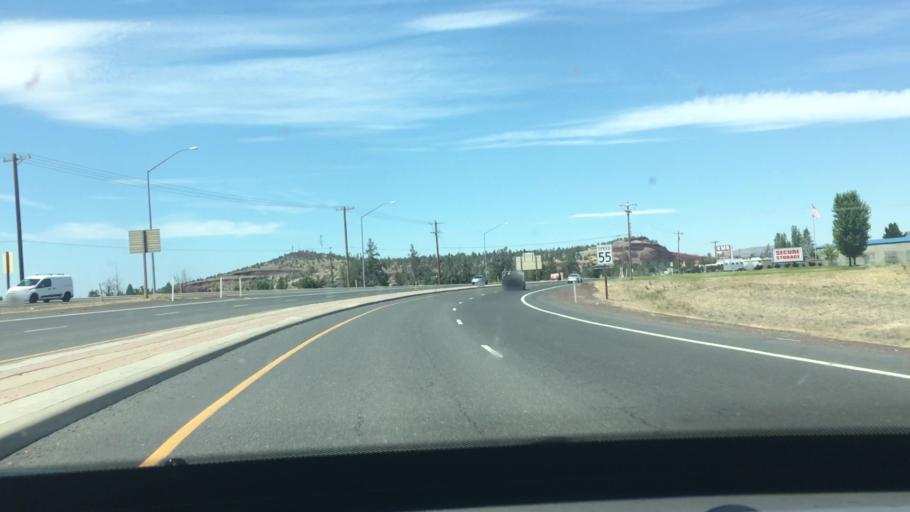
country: US
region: Oregon
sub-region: Deschutes County
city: Redmond
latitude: 44.3026
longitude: -121.1730
